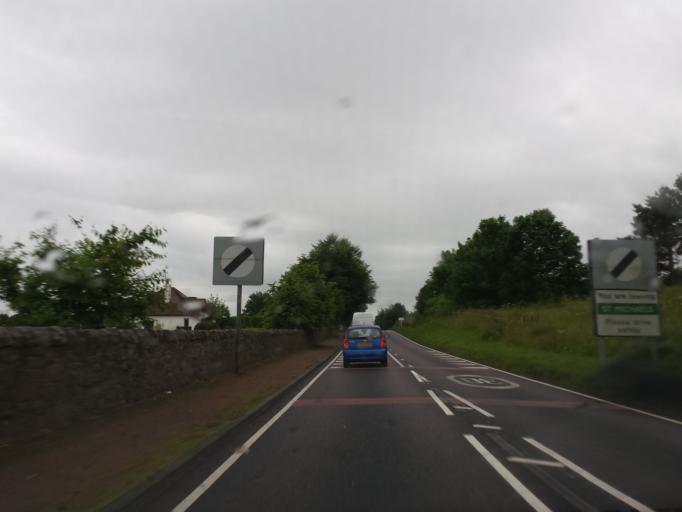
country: GB
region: Scotland
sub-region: Fife
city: Leuchars
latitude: 56.3922
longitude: -2.9032
